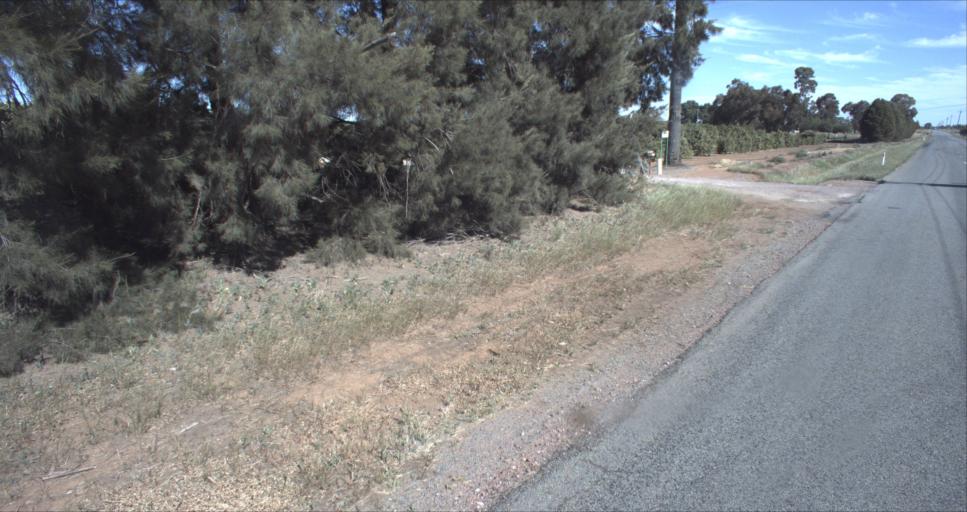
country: AU
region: New South Wales
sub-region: Leeton
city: Leeton
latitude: -34.5666
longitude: 146.3825
